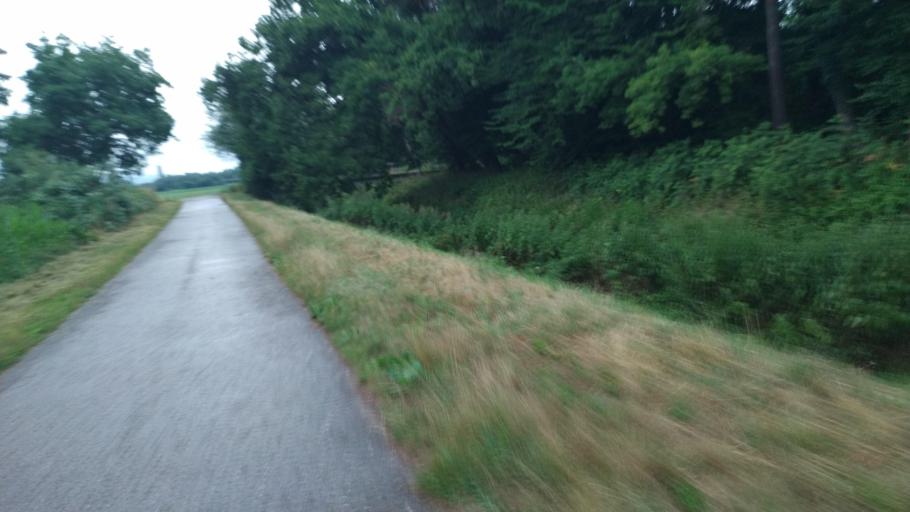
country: DE
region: Baden-Wuerttemberg
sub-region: Karlsruhe Region
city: Ettlingen
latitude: 48.9693
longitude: 8.3851
